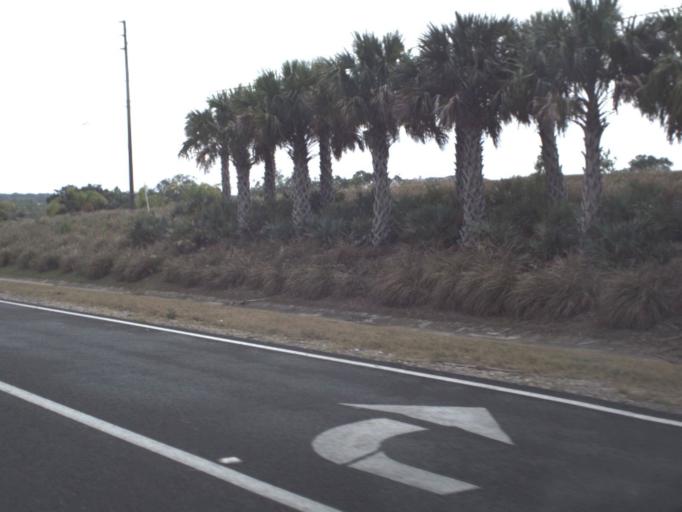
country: US
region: Florida
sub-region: Lake County
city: Clermont
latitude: 28.5580
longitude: -81.8084
